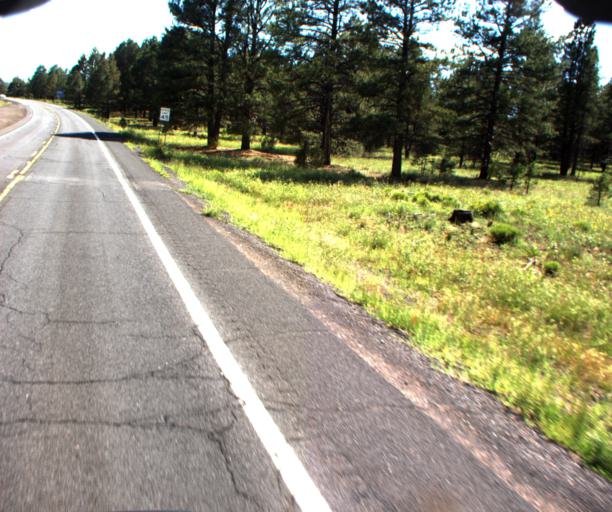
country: US
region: Arizona
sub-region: Coconino County
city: Williams
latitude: 35.2669
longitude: -112.1499
